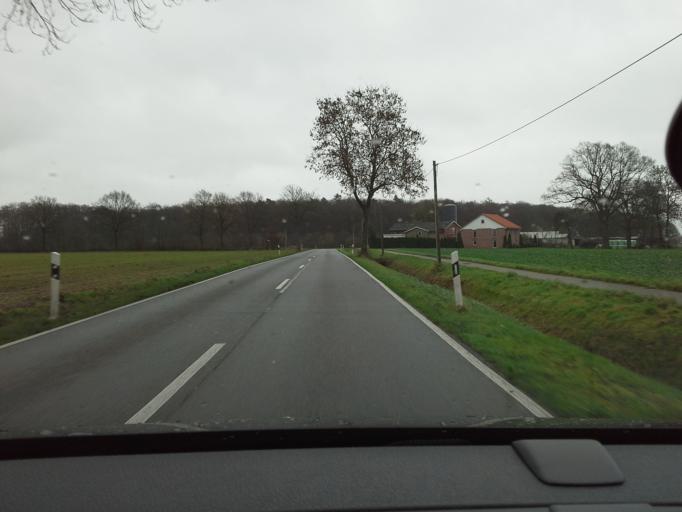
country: DE
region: Schleswig-Holstein
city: Bilsen
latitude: 53.7579
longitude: 9.8666
